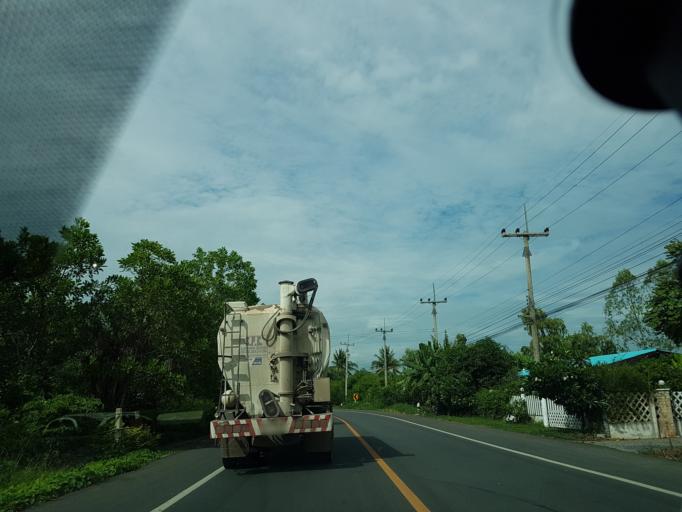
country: TH
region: Lop Buri
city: Tha Wung
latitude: 14.7687
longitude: 100.5662
